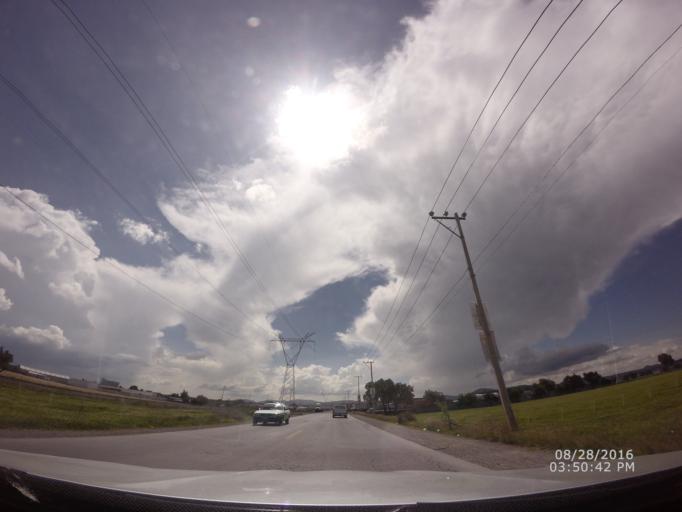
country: MX
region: Hidalgo
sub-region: Mineral de la Reforma
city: Los Tuzos
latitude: 20.0371
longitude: -98.7360
